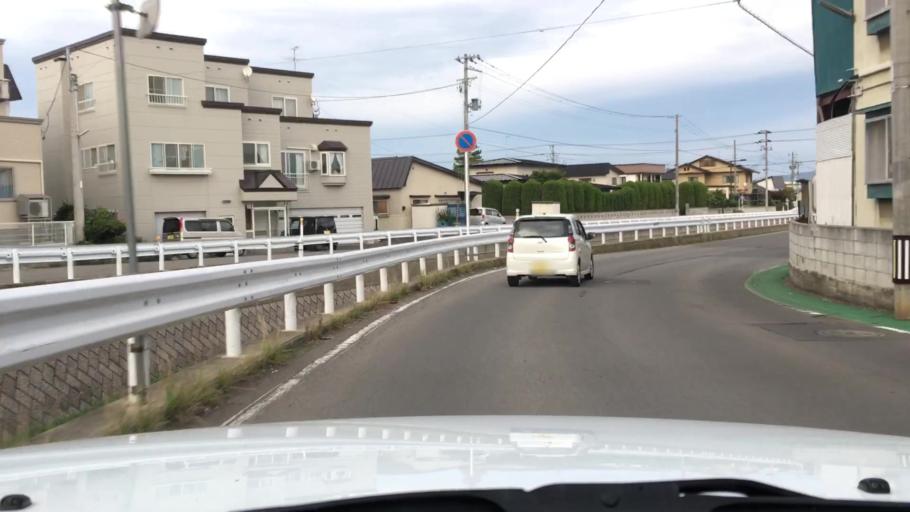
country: JP
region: Aomori
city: Hirosaki
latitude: 40.5941
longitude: 140.4942
